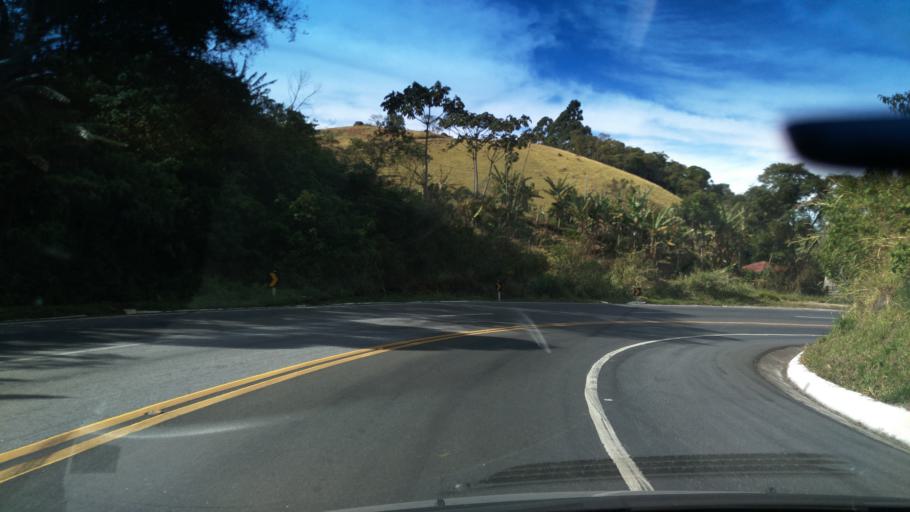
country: BR
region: Minas Gerais
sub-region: Borda Da Mata
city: Borda da Mata
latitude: -22.1308
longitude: -46.1743
